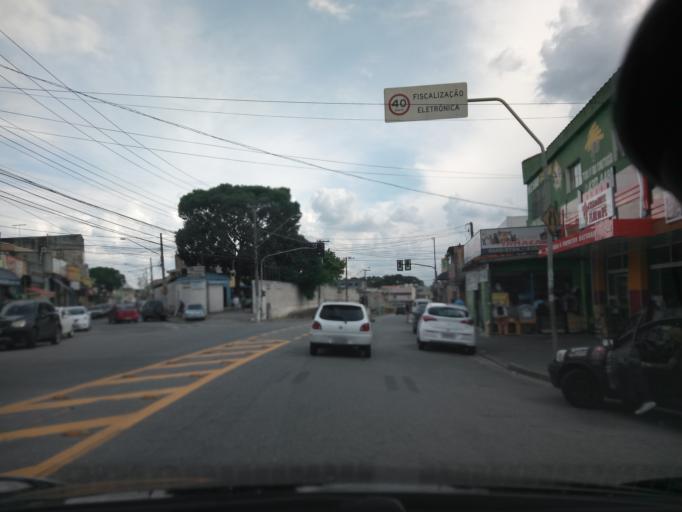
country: BR
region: Sao Paulo
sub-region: Sao Bernardo Do Campo
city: Sao Bernardo do Campo
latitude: -23.7398
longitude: -46.5699
